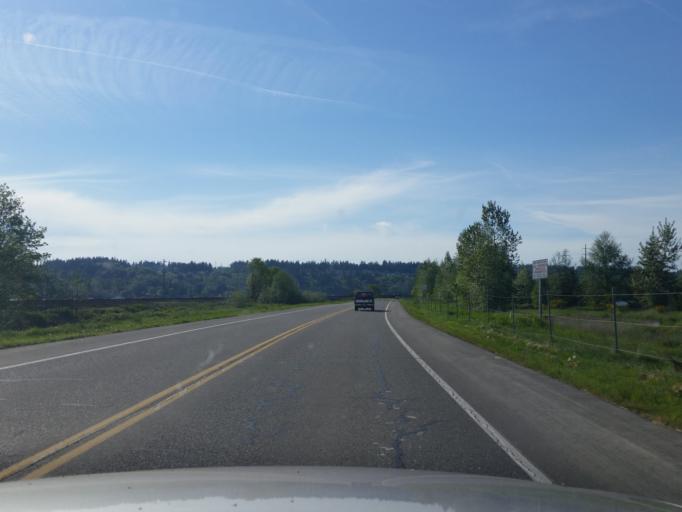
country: US
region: Washington
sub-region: Snohomish County
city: Fobes Hill
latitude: 47.9248
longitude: -122.1624
